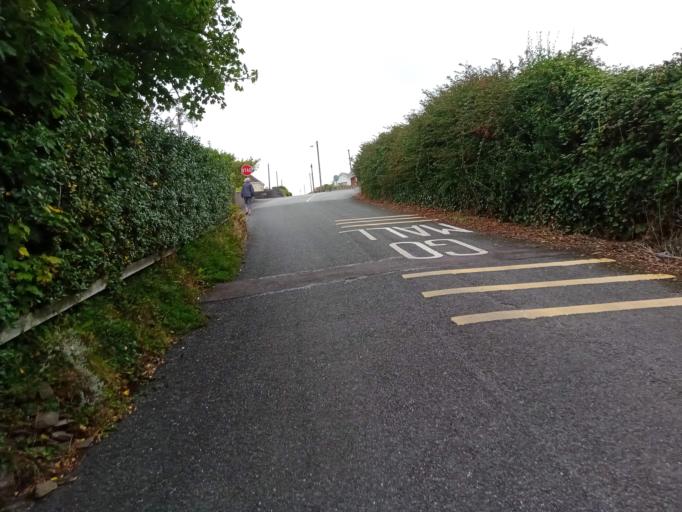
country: IE
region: Munster
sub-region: Waterford
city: Dungarvan
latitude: 52.0482
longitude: -7.5654
